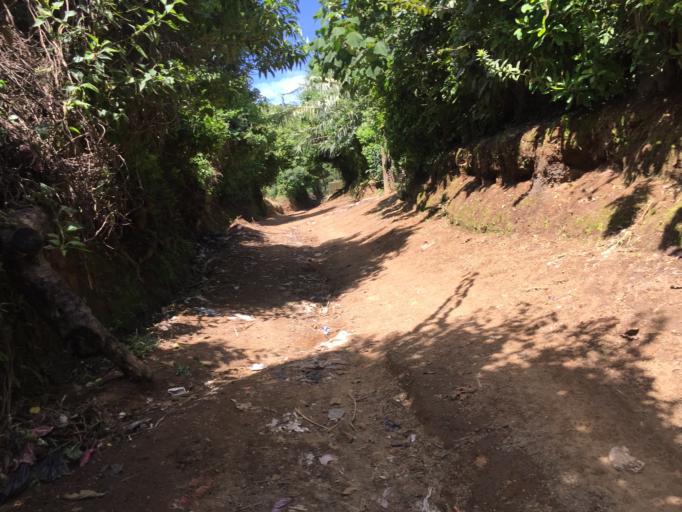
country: GT
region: Sacatepequez
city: Magdalena Milpas Altas
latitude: 14.5104
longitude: -90.6573
